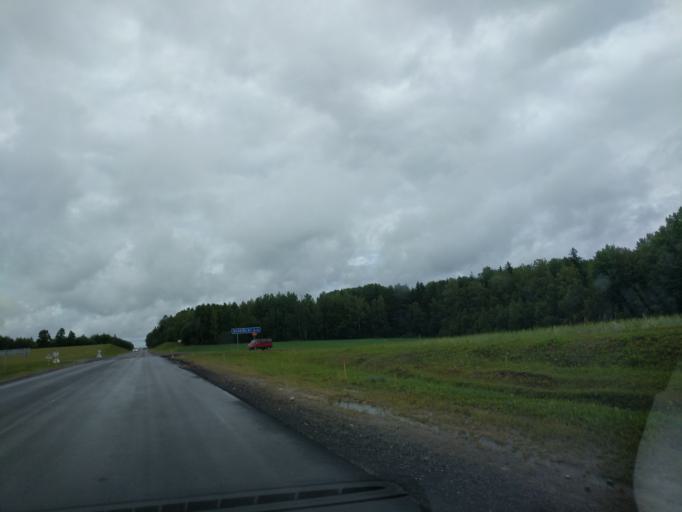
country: BY
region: Minsk
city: Il'ya
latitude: 54.3091
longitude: 27.4728
